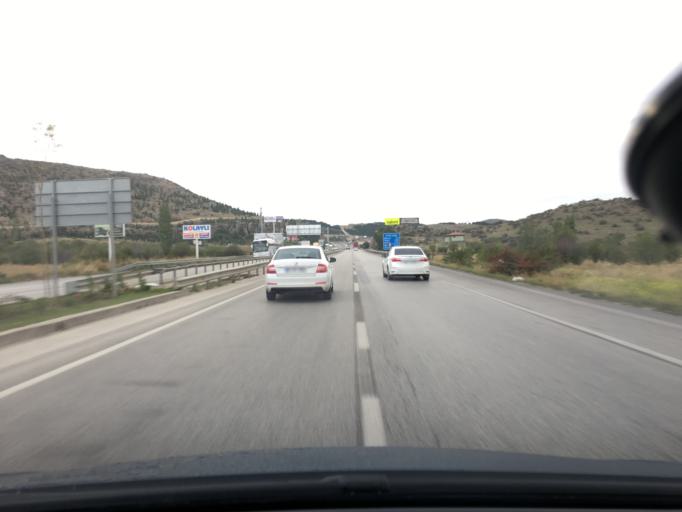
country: TR
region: Afyonkarahisar
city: Afyonkarahisar
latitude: 38.7920
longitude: 30.4512
